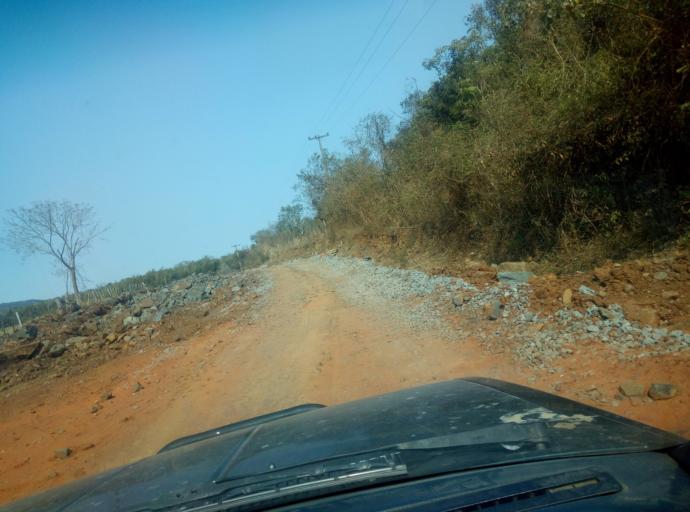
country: PY
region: Caaguazu
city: Coronel Oviedo
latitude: -25.3360
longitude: -56.3147
